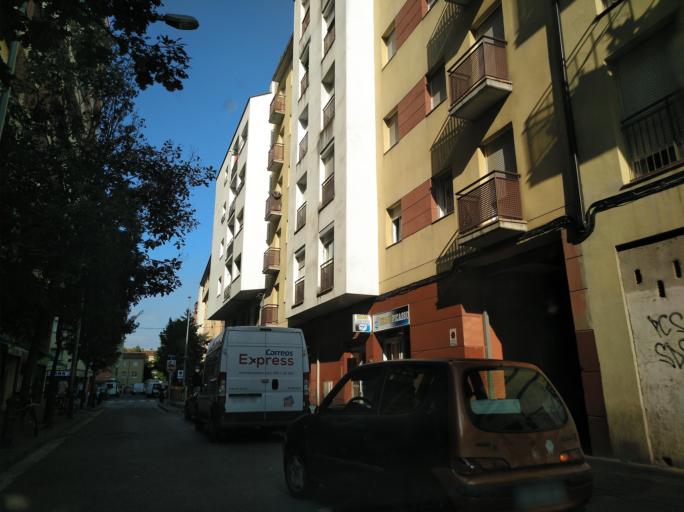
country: ES
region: Catalonia
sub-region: Provincia de Girona
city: Salt
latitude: 41.9734
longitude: 2.7911
